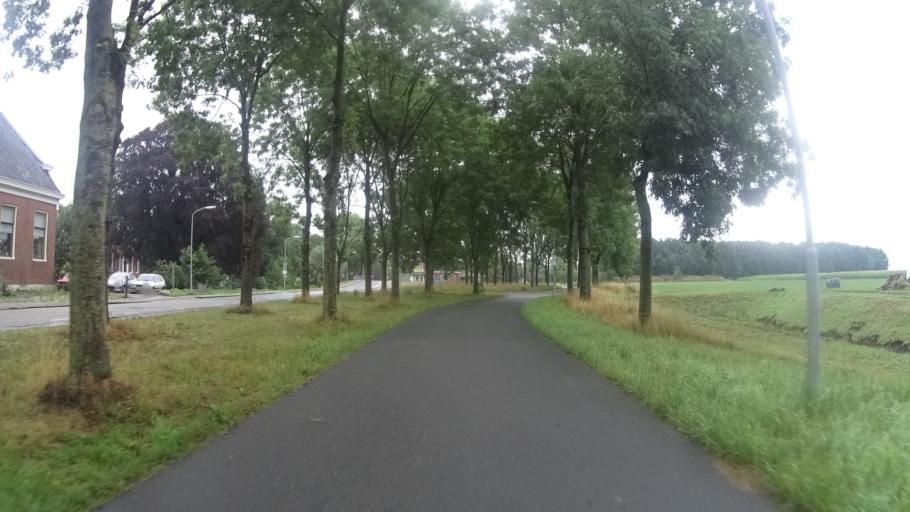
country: NL
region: Groningen
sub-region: Gemeente  Oldambt
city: Winschoten
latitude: 53.1679
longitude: 7.0895
